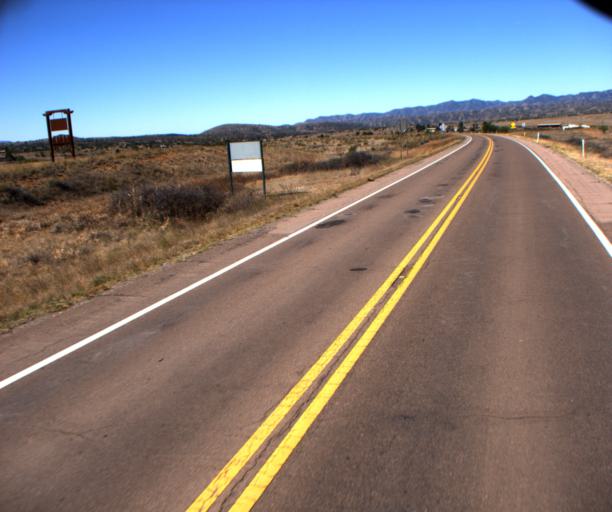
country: US
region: Arizona
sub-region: Pima County
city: Corona de Tucson
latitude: 31.6783
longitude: -110.6619
